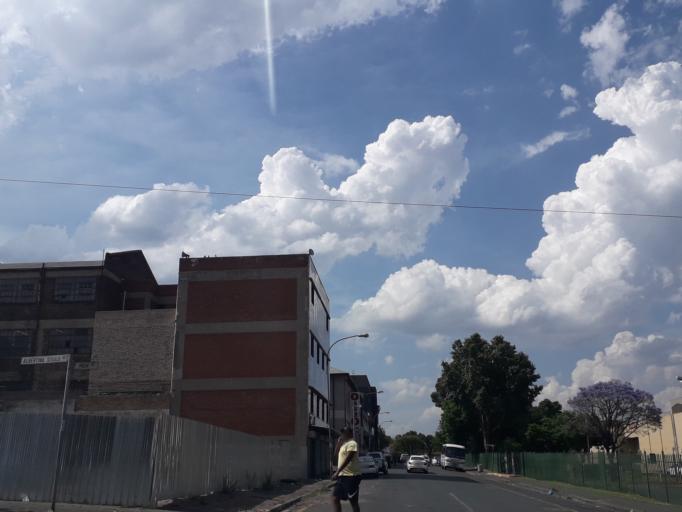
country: ZA
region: Gauteng
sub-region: City of Johannesburg Metropolitan Municipality
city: Johannesburg
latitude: -26.2059
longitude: 28.0235
